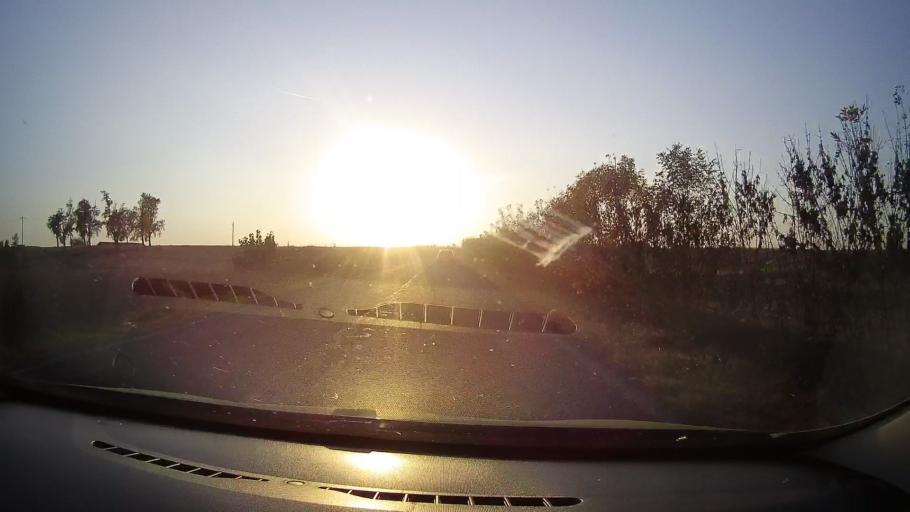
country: RO
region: Arad
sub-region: Comuna Bocsig
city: Bocsig
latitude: 46.4191
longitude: 21.9656
